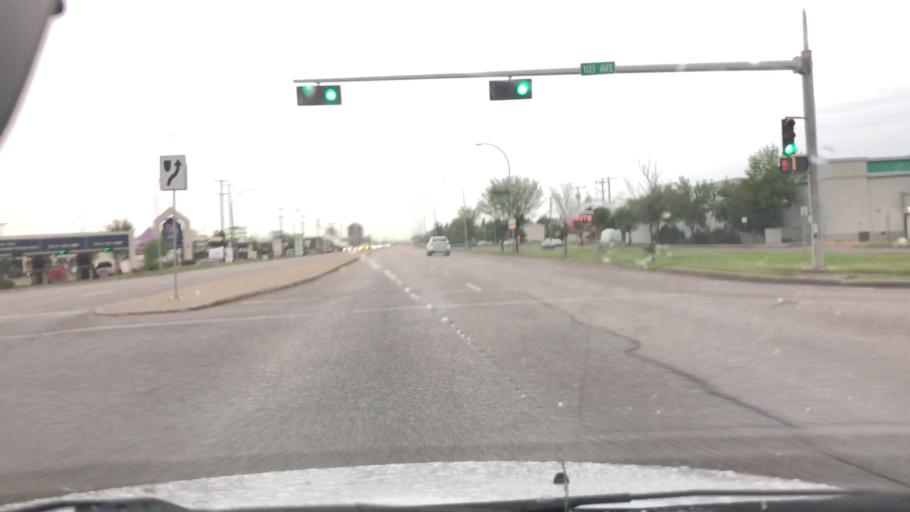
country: CA
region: Alberta
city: St. Albert
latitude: 53.5449
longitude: -113.6139
